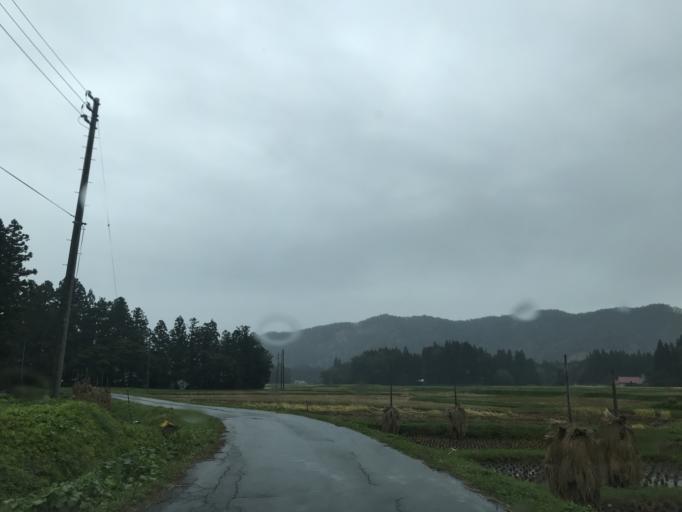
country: JP
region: Iwate
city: Ichinoseki
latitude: 38.9779
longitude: 140.9569
